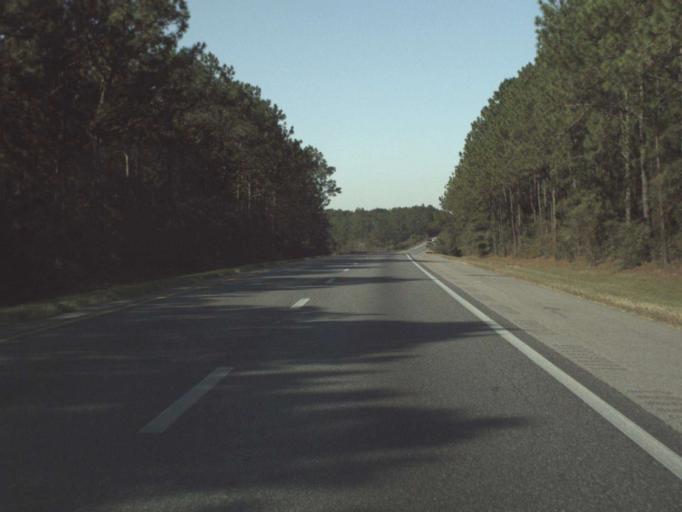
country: US
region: Florida
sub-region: Okaloosa County
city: Crestview
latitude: 30.7152
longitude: -86.6173
